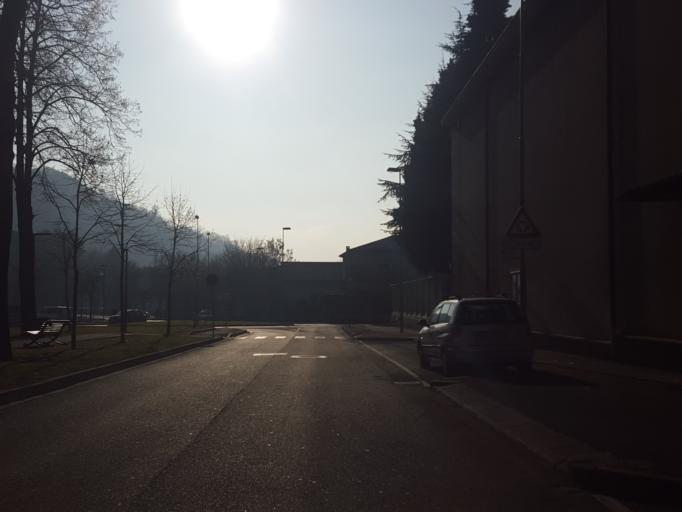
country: IT
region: Veneto
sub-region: Provincia di Vicenza
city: Valdagno
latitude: 45.6489
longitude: 11.3052
